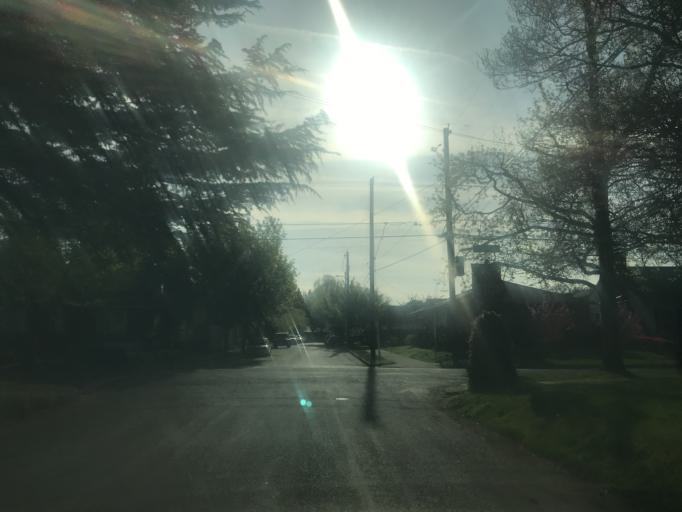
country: US
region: Oregon
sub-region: Multnomah County
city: Lents
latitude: 45.5034
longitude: -122.5921
